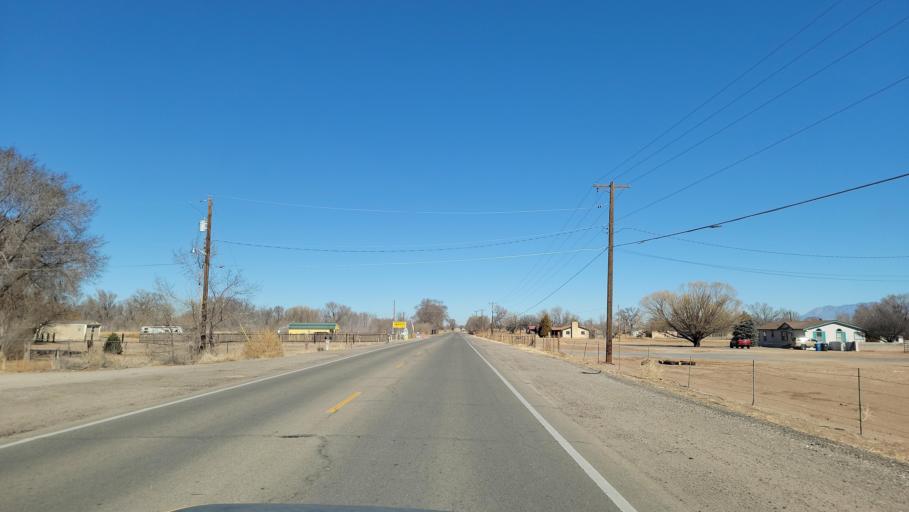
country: US
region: New Mexico
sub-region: Valencia County
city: Bosque Farms
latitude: 34.9250
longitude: -106.6928
